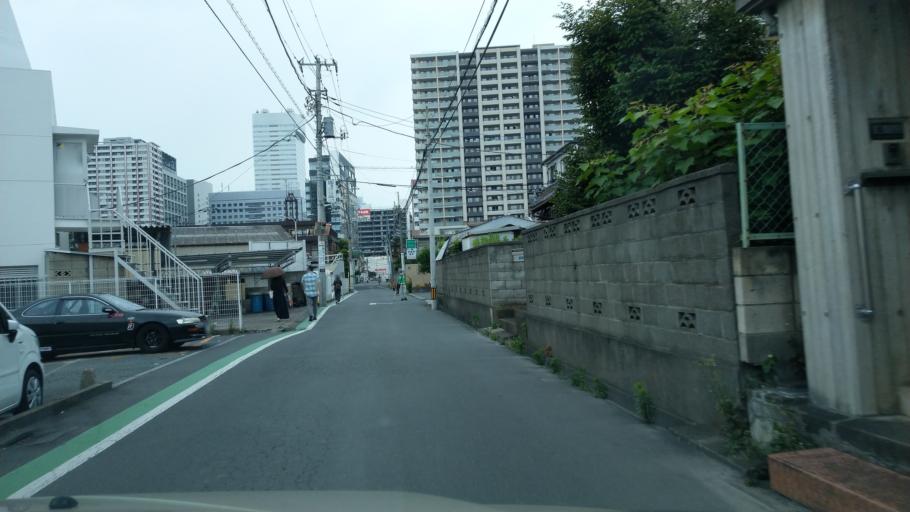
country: JP
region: Saitama
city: Yono
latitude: 35.9005
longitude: 139.6231
